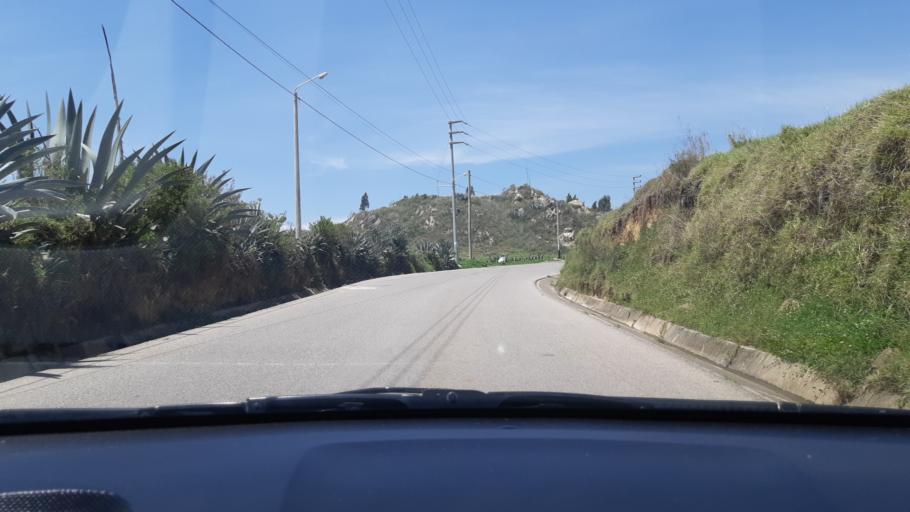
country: PE
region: Cajamarca
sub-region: Provincia de Cajamarca
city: Llacanora
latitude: -7.1756
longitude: -78.4578
